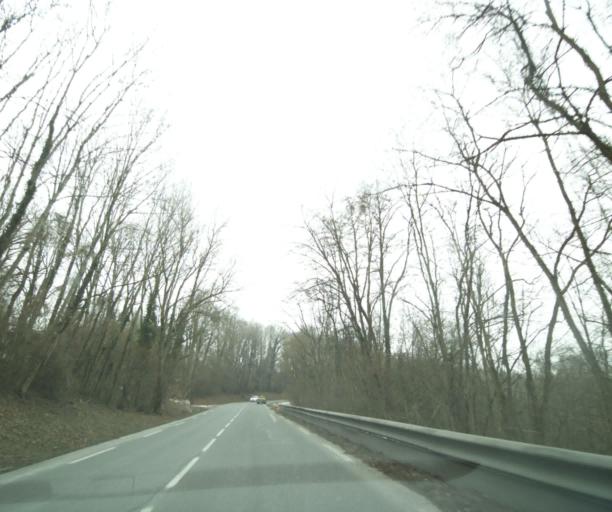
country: FR
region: Rhone-Alpes
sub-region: Departement de la Haute-Savoie
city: Reignier-Esery
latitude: 46.1430
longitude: 6.2695
